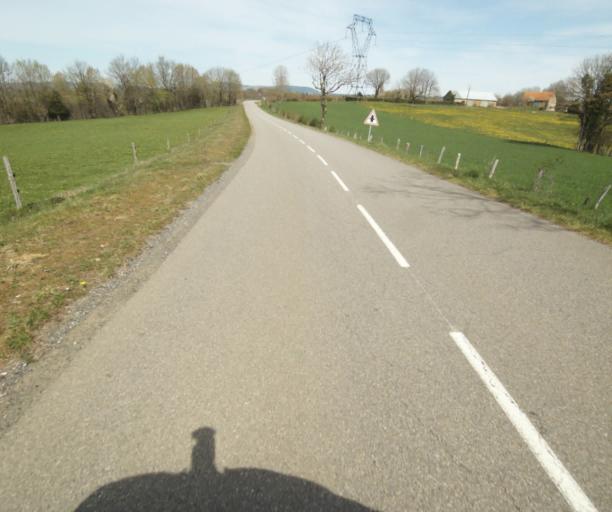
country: FR
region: Limousin
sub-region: Departement de la Correze
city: Naves
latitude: 45.3696
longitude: 1.7987
